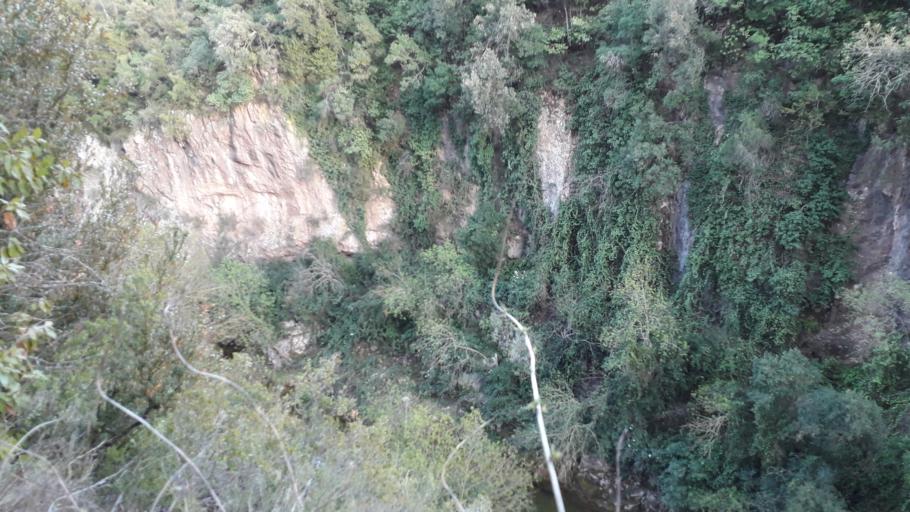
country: ES
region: Catalonia
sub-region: Provincia de Barcelona
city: Orpi
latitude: 41.5194
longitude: 1.5617
